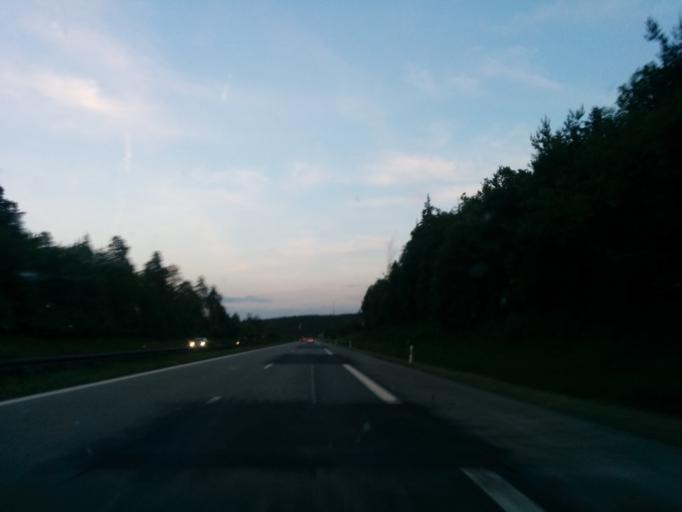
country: DE
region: Baden-Wuerttemberg
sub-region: Regierungsbezirk Stuttgart
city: Ellenberg
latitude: 49.0383
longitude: 10.1851
